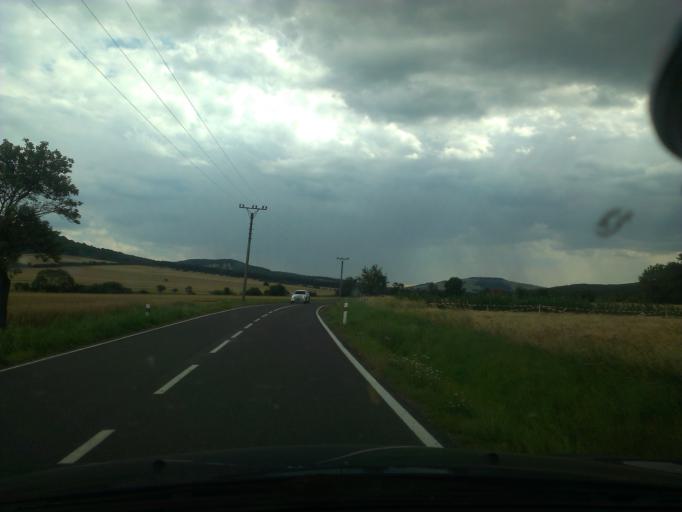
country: CZ
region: South Moravian
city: Velka nad Velickou
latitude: 48.8570
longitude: 17.5227
